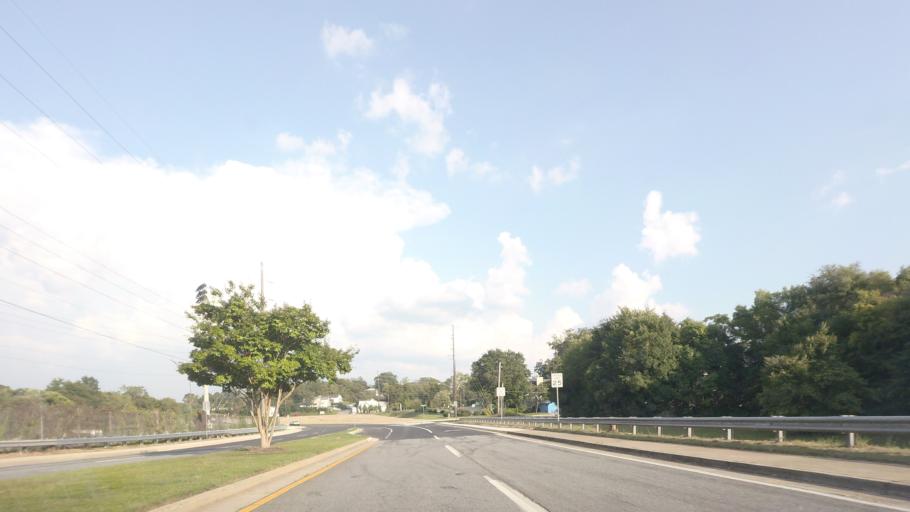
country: US
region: Georgia
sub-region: Bibb County
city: Macon
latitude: 32.8258
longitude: -83.6458
